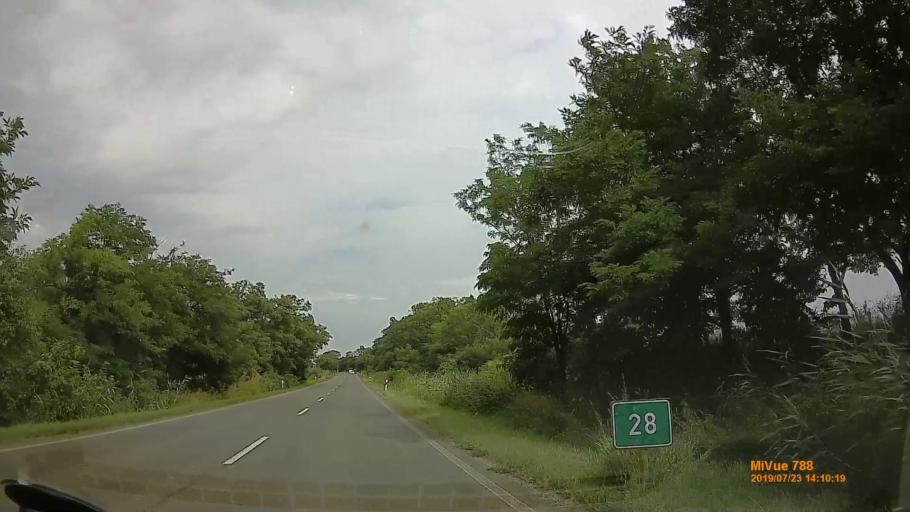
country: HU
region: Szabolcs-Szatmar-Bereg
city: Tiszavasvari
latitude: 47.9585
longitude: 21.4139
